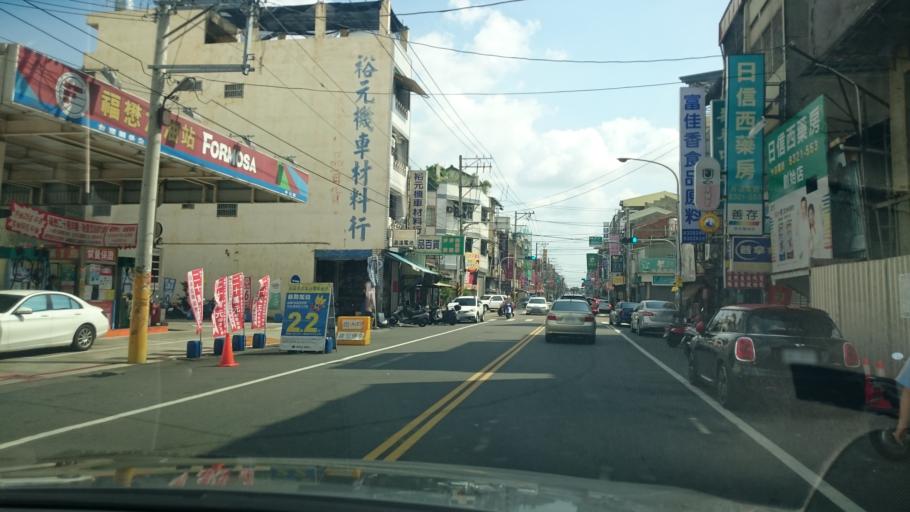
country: TW
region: Taiwan
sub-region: Nantou
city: Nantou
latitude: 23.9558
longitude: 120.5689
